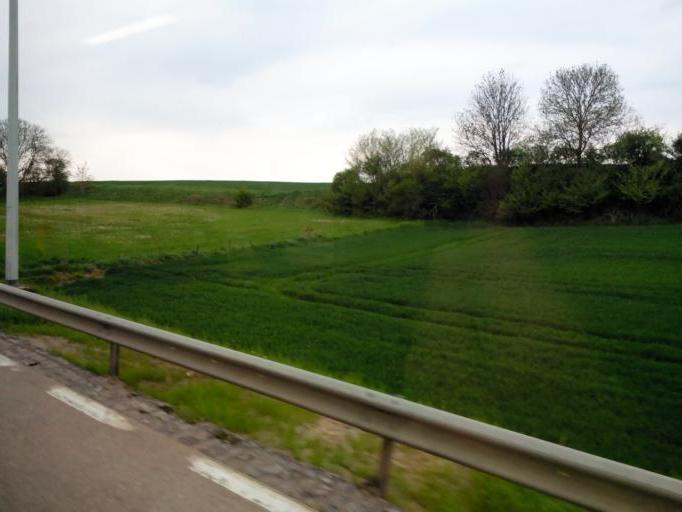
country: BE
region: Flanders
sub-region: Provincie Vlaams-Brabant
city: Herent
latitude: 50.8893
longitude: 4.6562
